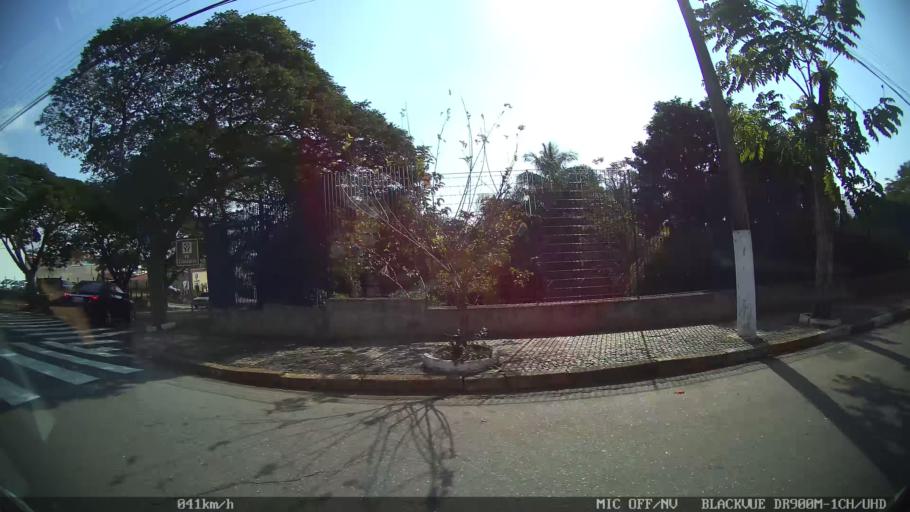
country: BR
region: Sao Paulo
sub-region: Paulinia
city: Paulinia
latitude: -22.7655
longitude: -47.1531
